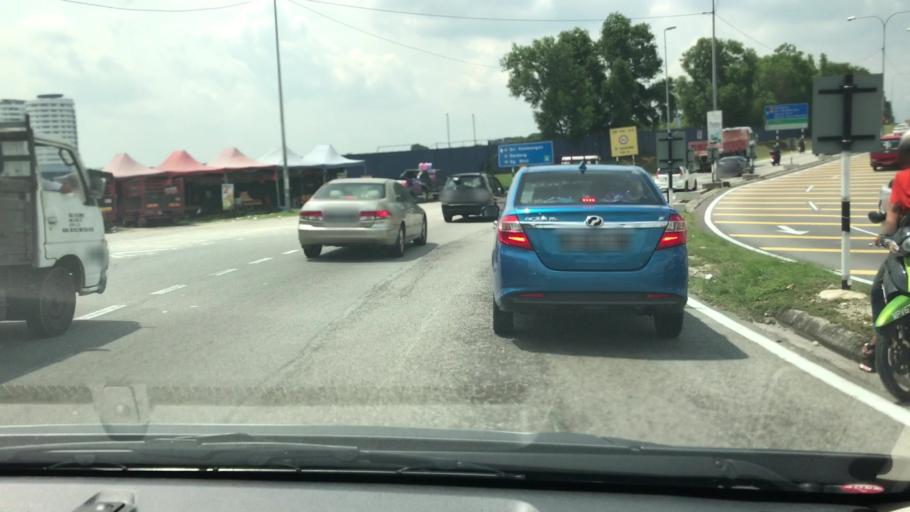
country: MY
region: Putrajaya
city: Putrajaya
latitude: 2.9817
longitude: 101.6583
